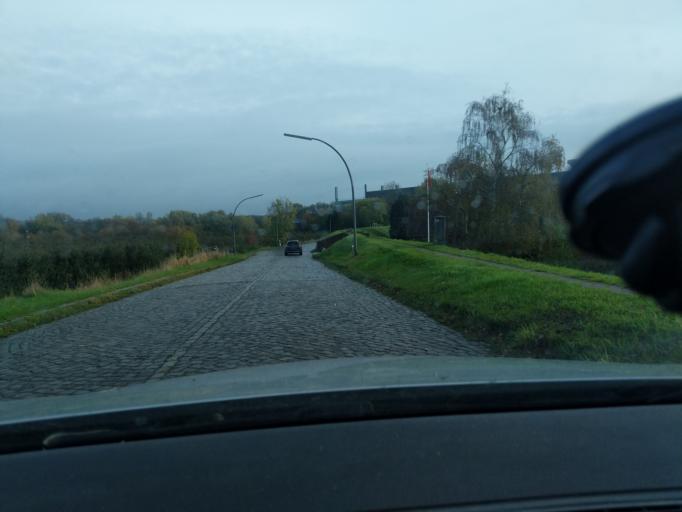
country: DE
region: Lower Saxony
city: Neu Wulmstorf
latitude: 53.5320
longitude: 9.7787
